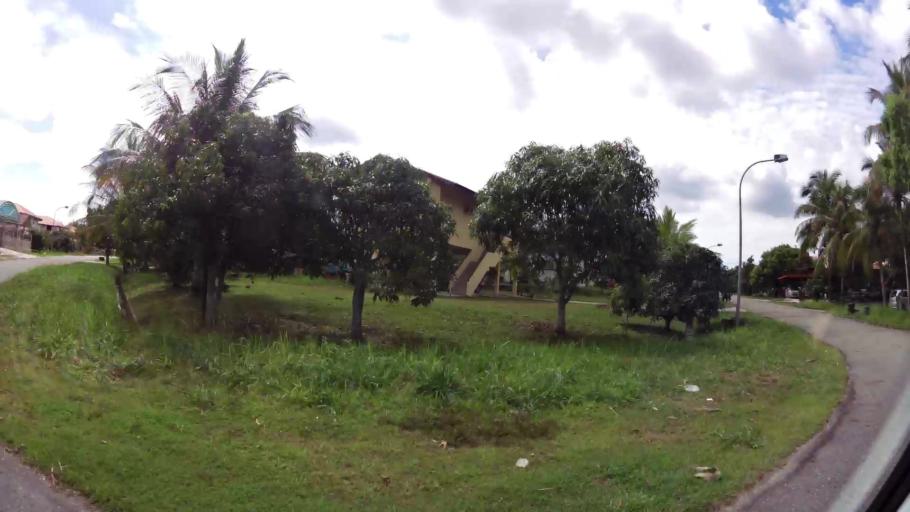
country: BN
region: Brunei and Muara
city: Bandar Seri Begawan
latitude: 4.9391
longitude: 114.8985
